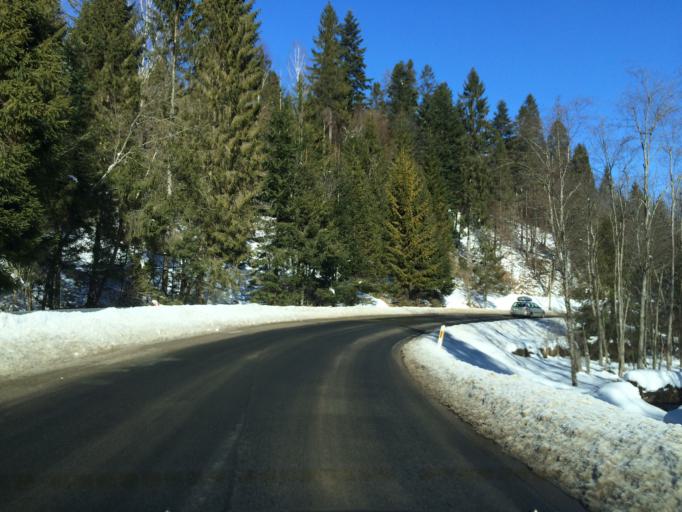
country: PL
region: Subcarpathian Voivodeship
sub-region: Powiat leski
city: Cisna
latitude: 49.2134
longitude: 22.3627
